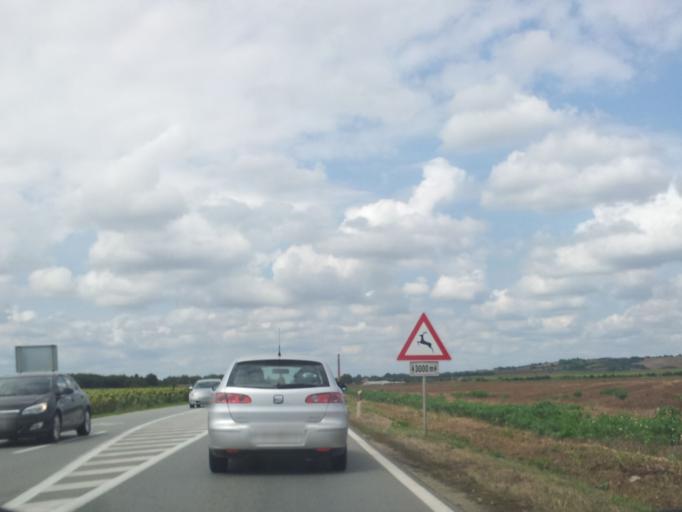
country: HR
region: Osjecko-Baranjska
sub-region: Grad Osijek
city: Karanac
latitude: 45.7430
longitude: 18.6500
